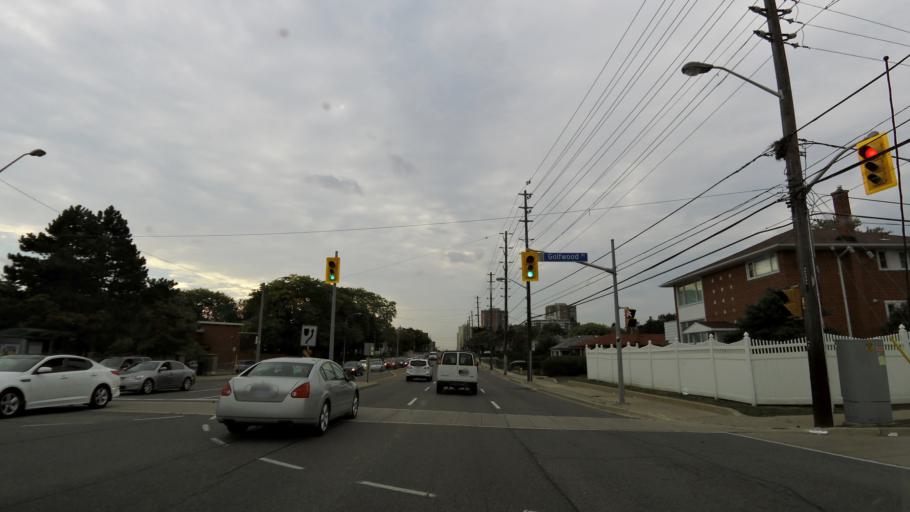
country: CA
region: Ontario
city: Etobicoke
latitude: 43.6986
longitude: -79.5398
